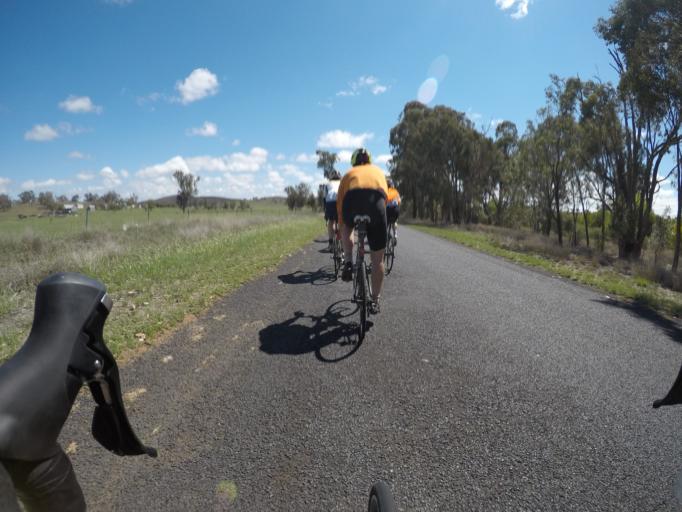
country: AU
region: New South Wales
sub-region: Dubbo Municipality
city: Dubbo
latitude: -32.5658
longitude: 148.5363
